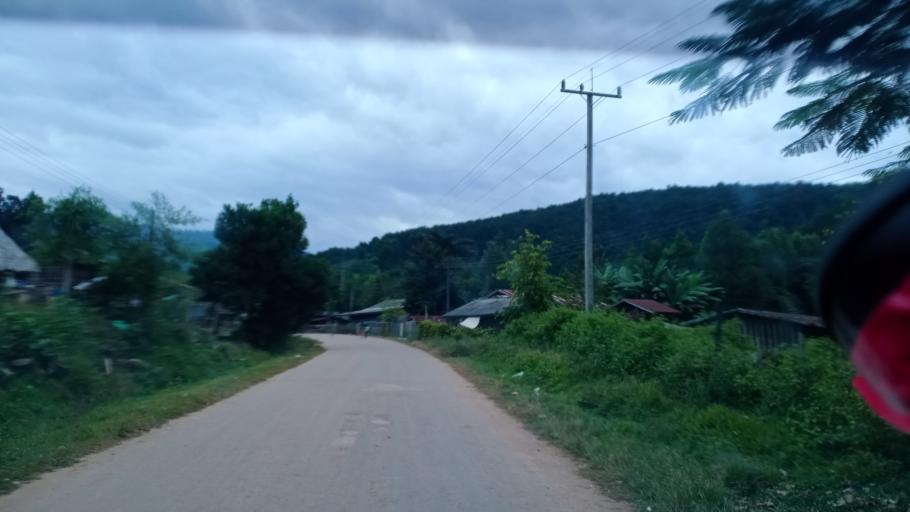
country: TH
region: Changwat Bueng Kan
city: Pak Khat
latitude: 18.7118
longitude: 103.2116
